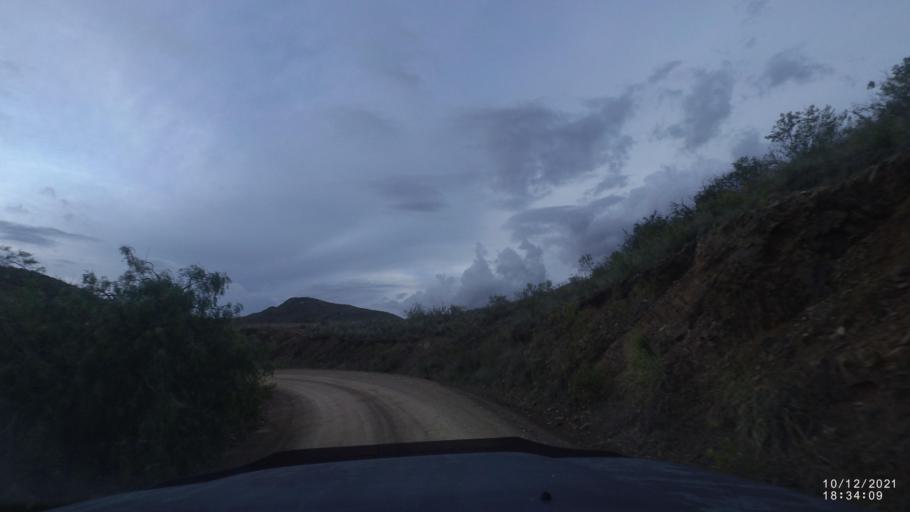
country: BO
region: Cochabamba
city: Tarata
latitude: -17.8233
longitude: -65.9876
